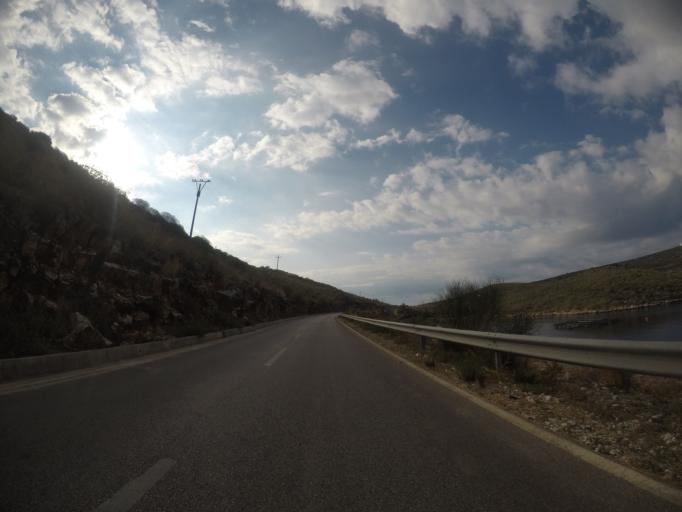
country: AL
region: Vlore
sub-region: Rrethi i Vlores
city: Himare
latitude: 40.0554
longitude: 19.8036
